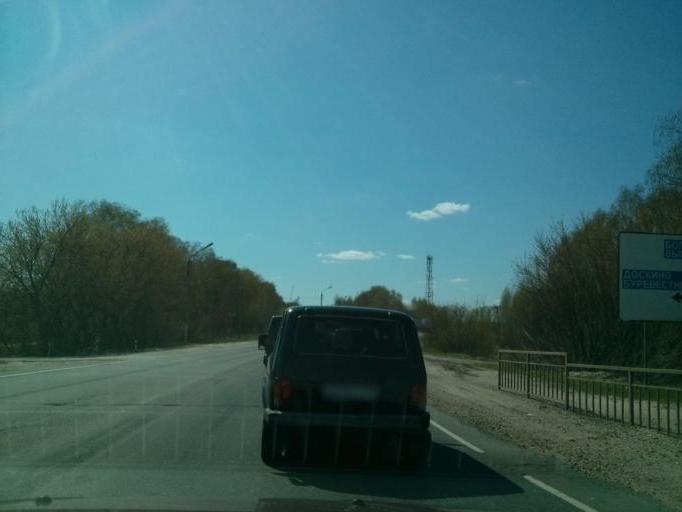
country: RU
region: Nizjnij Novgorod
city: Burevestnik
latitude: 56.1754
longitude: 43.7681
